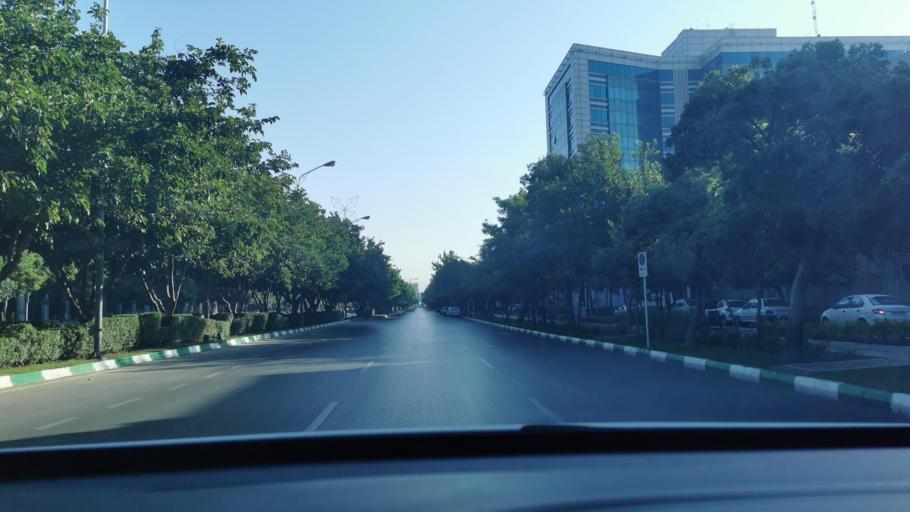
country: IR
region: Razavi Khorasan
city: Mashhad
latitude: 36.2938
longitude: 59.5603
